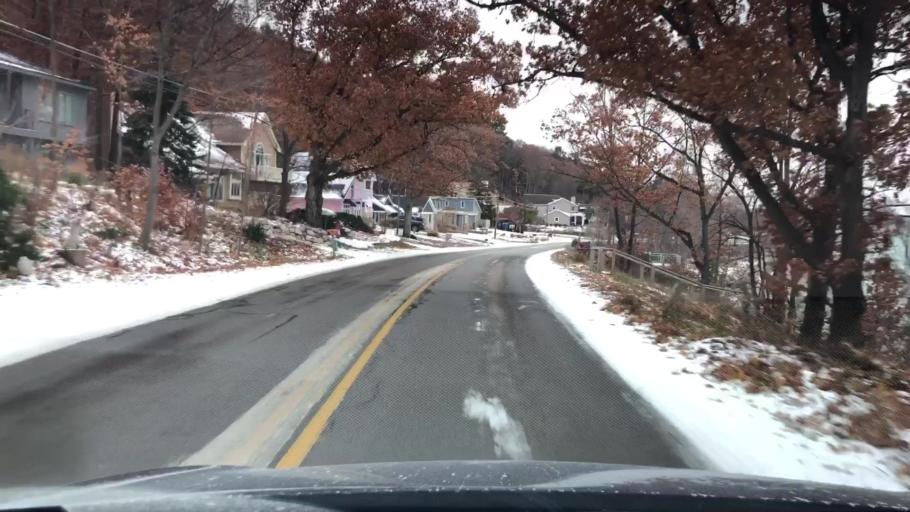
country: US
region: Michigan
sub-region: Grand Traverse County
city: Traverse City
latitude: 44.8030
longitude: -85.5813
